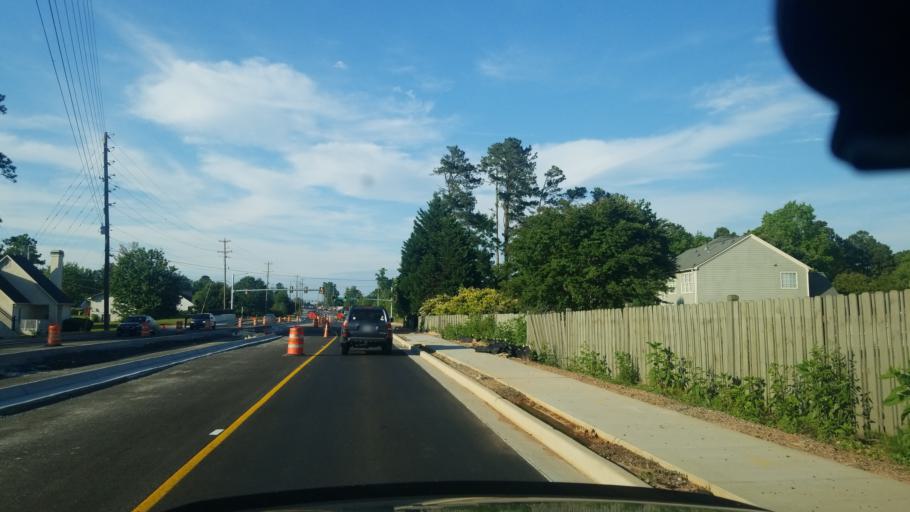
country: US
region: Georgia
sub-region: Fulton County
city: Johns Creek
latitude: 34.0893
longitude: -84.1813
